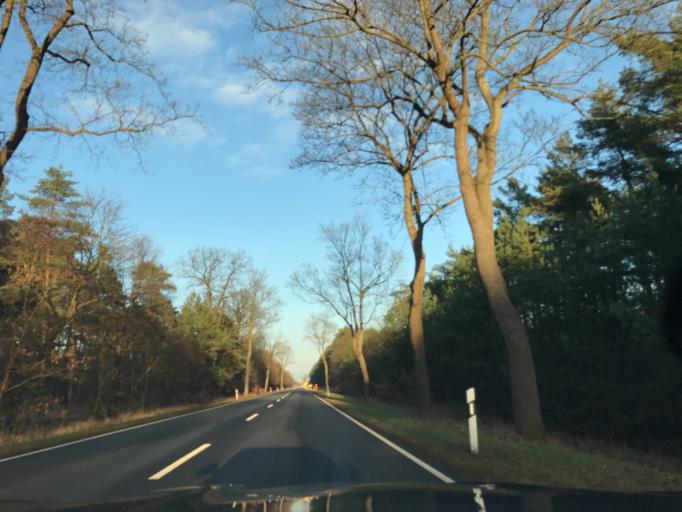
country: DE
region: Saxony-Anhalt
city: Genthin
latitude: 52.3853
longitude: 12.1288
